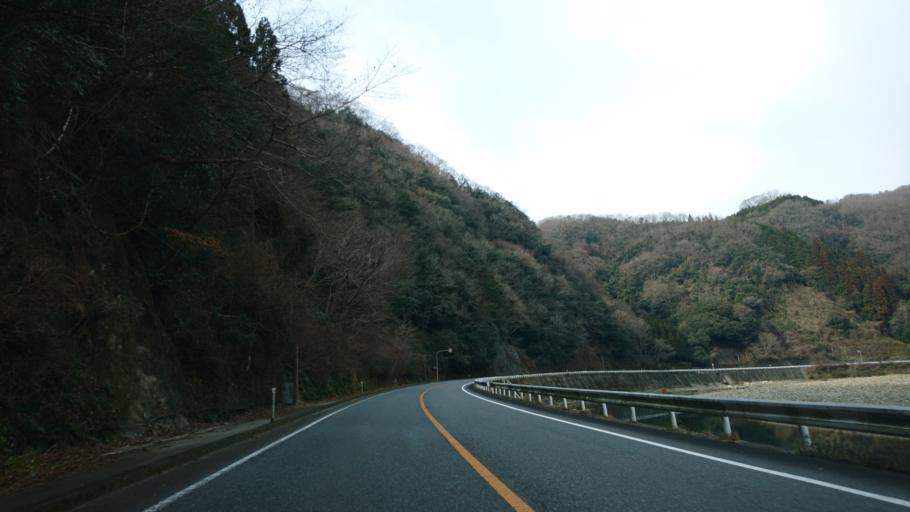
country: JP
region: Okayama
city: Takahashi
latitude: 34.8601
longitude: 133.5651
